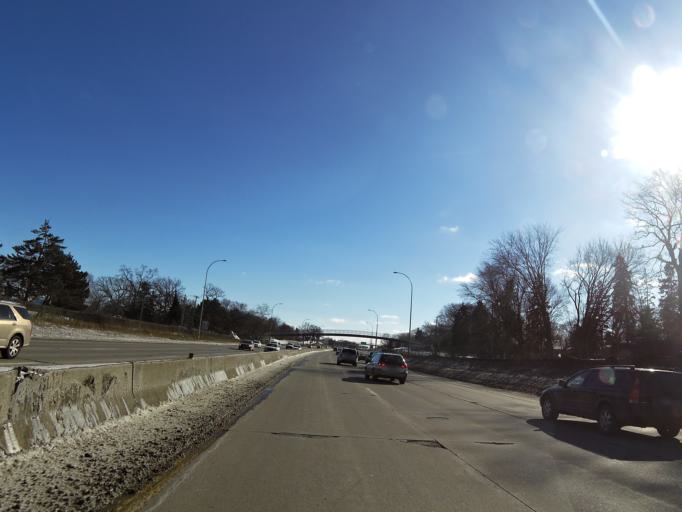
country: US
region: Minnesota
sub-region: Hennepin County
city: Edina
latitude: 44.9066
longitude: -93.3502
